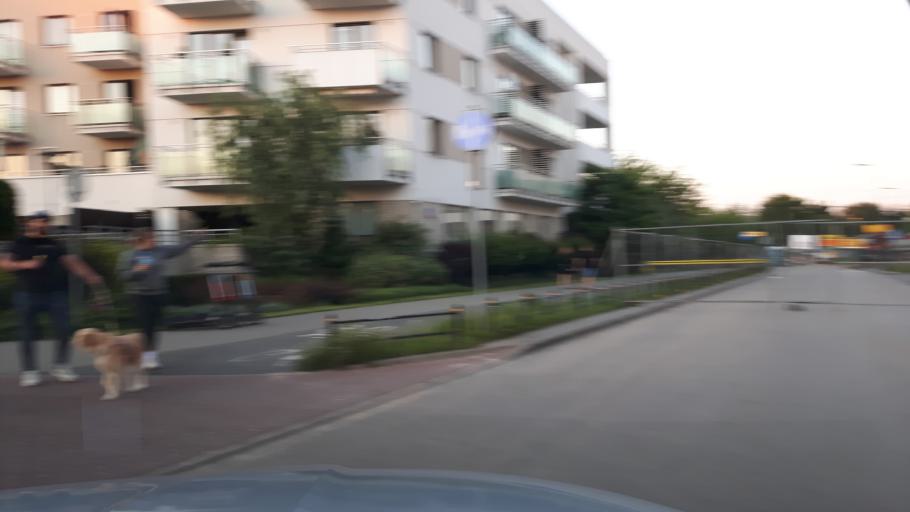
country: PL
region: Masovian Voivodeship
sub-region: Warszawa
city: Mokotow
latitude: 52.2093
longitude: 21.0654
